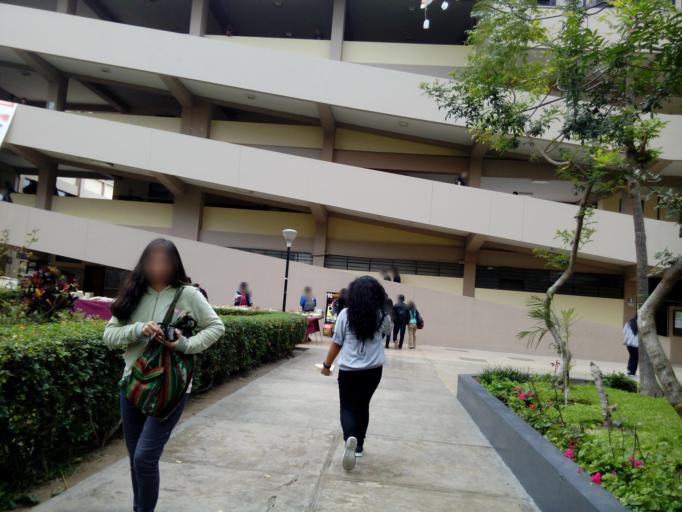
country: PE
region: Callao
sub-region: Callao
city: Callao
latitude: -12.0584
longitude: -77.0834
